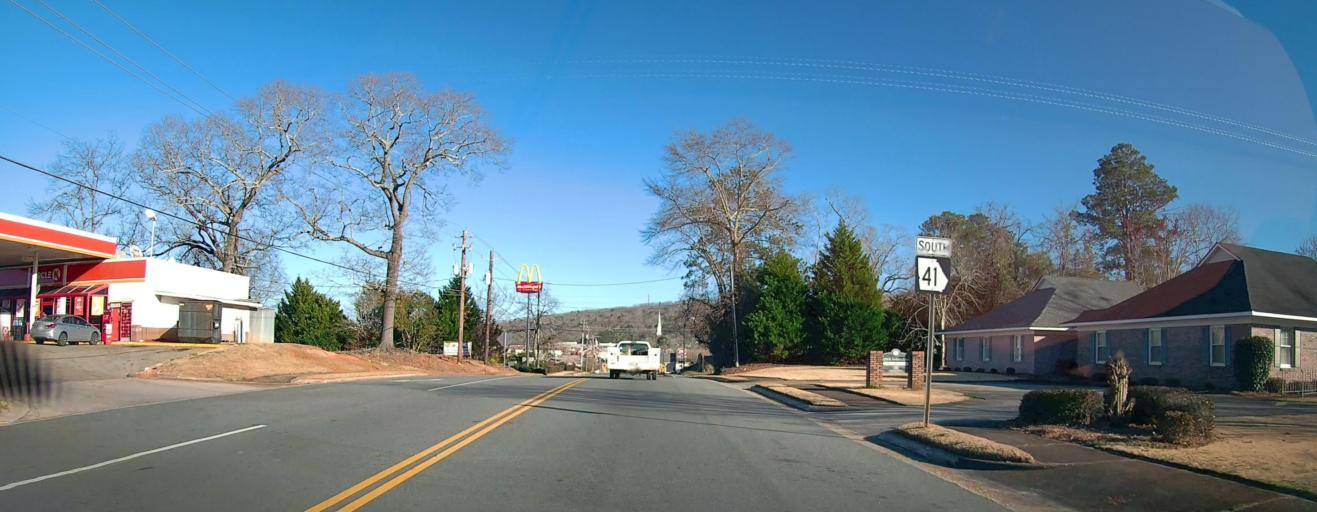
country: US
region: Georgia
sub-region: Meriwether County
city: Manchester
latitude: 32.8537
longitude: -84.6200
